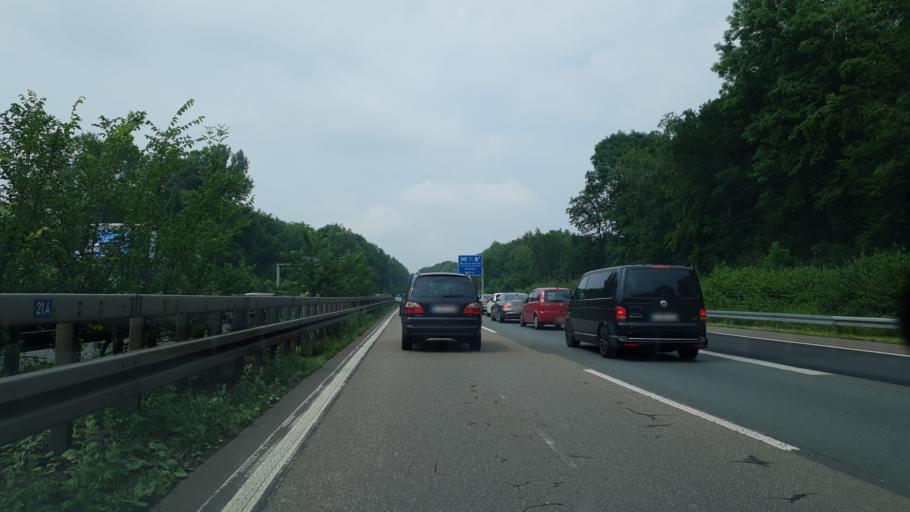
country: DE
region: North Rhine-Westphalia
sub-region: Regierungsbezirk Arnsberg
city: Bochum
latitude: 51.4818
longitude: 7.2788
